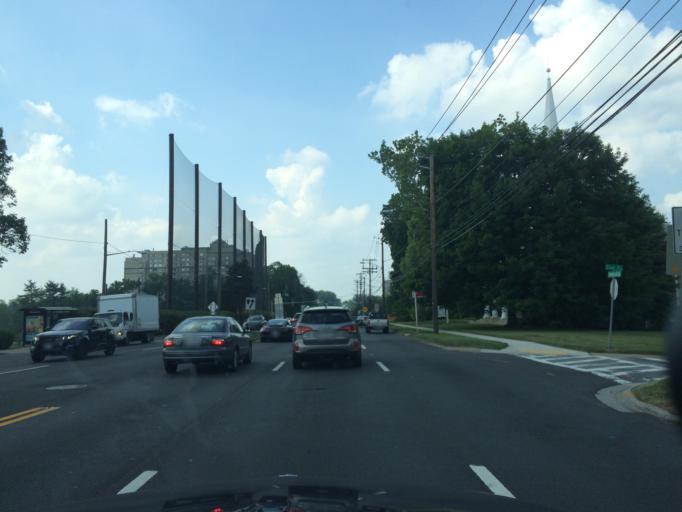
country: US
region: Maryland
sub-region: Montgomery County
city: Chevy Chase
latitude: 38.9887
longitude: -77.0771
